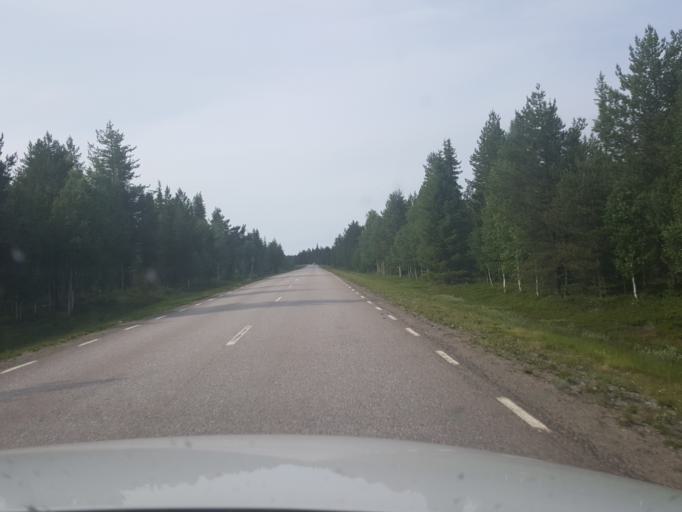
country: SE
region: Norrbotten
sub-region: Arjeplogs Kommun
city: Arjeplog
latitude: 65.7295
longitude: 18.0579
